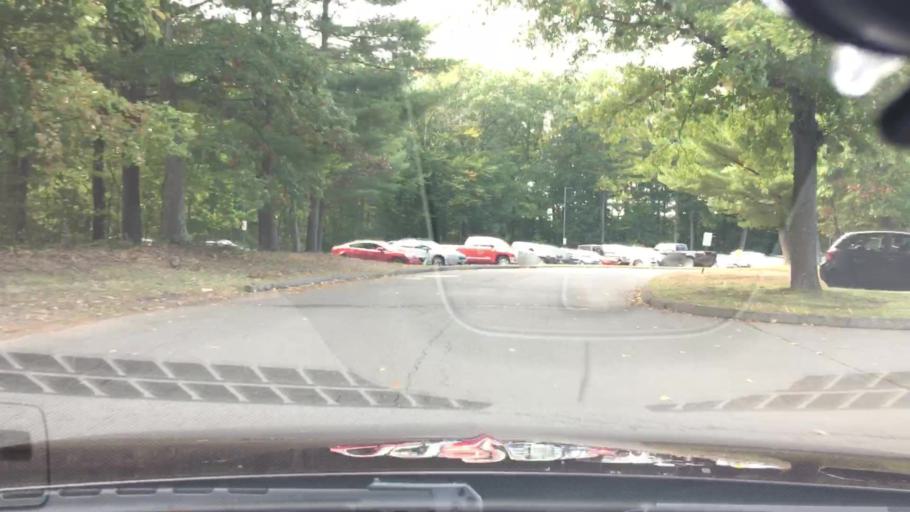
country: US
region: Connecticut
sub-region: Hartford County
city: Plainville
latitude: 41.6894
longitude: -72.8741
